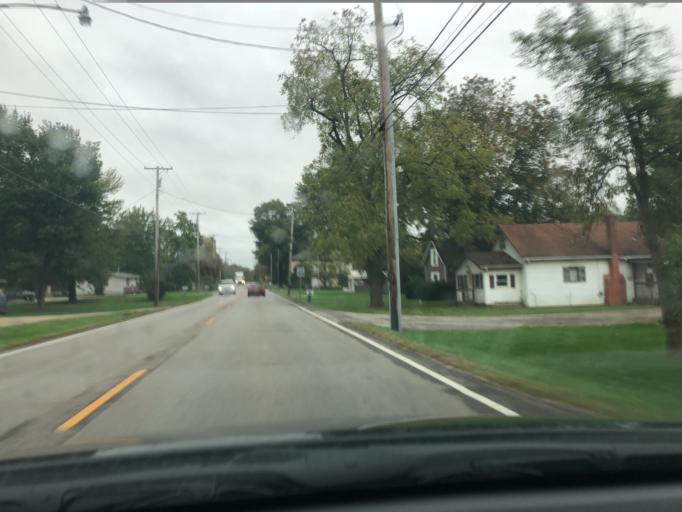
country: US
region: Ohio
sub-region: Union County
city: Marysville
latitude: 40.2470
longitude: -83.3039
